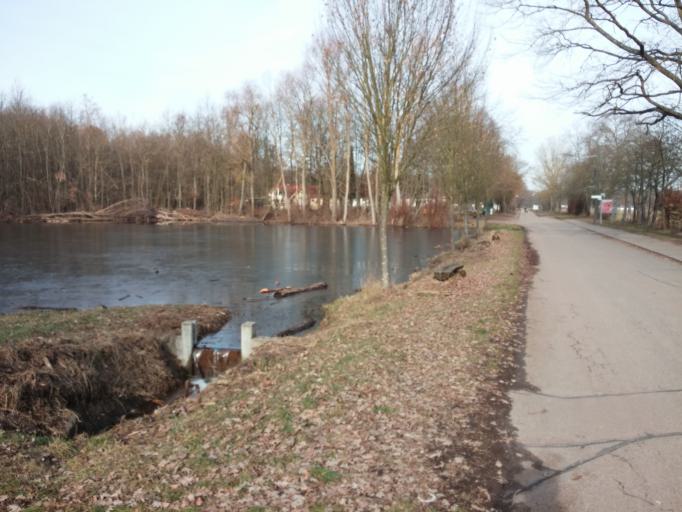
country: DE
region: Rheinland-Pfalz
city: Ottersheim
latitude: 49.1973
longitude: 8.2289
